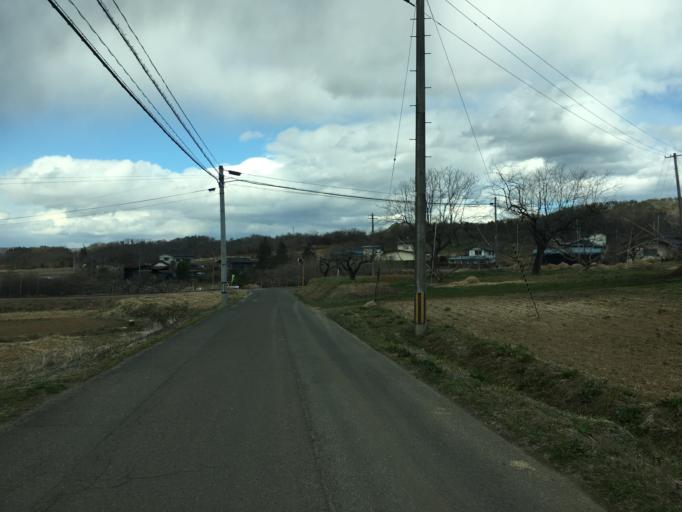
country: JP
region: Fukushima
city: Yanagawamachi-saiwaicho
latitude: 37.8386
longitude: 140.6099
